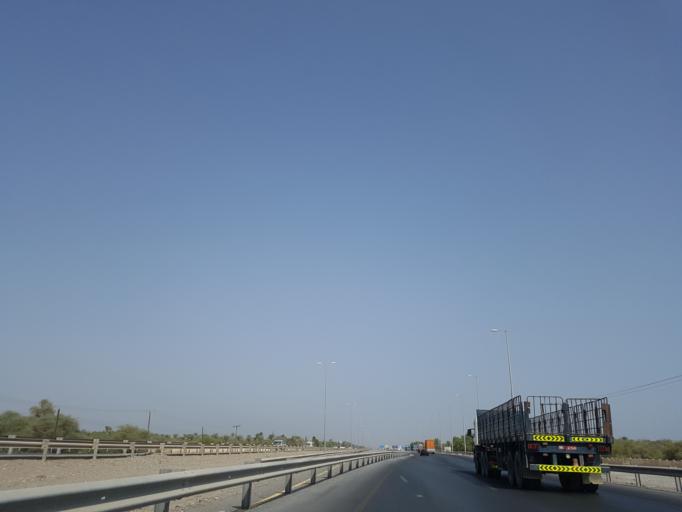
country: OM
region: Al Batinah
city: As Suwayq
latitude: 23.7578
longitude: 57.5596
